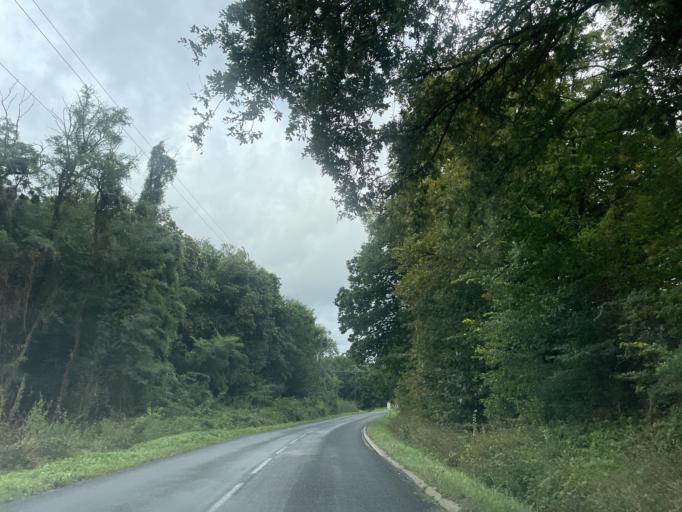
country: FR
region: Ile-de-France
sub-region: Departement de Seine-et-Marne
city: Saint-Jean-les-Deux-Jumeaux
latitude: 48.9350
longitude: 2.9885
